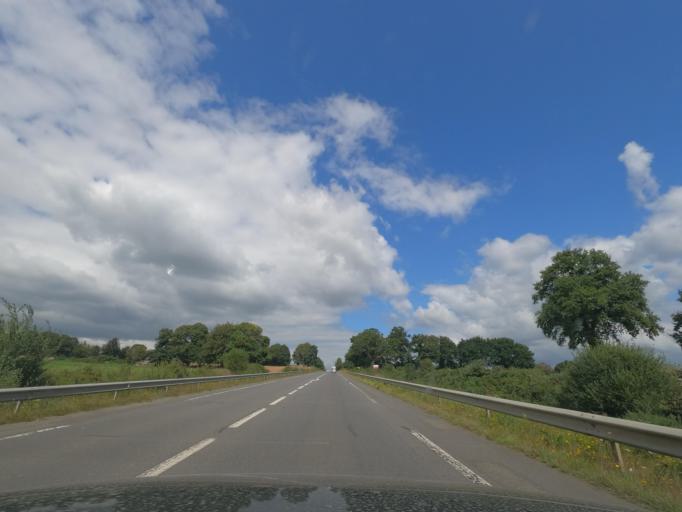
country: FR
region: Brittany
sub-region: Departement d'Ille-et-Vilaine
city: Lecousse
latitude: 48.3571
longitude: -1.2298
